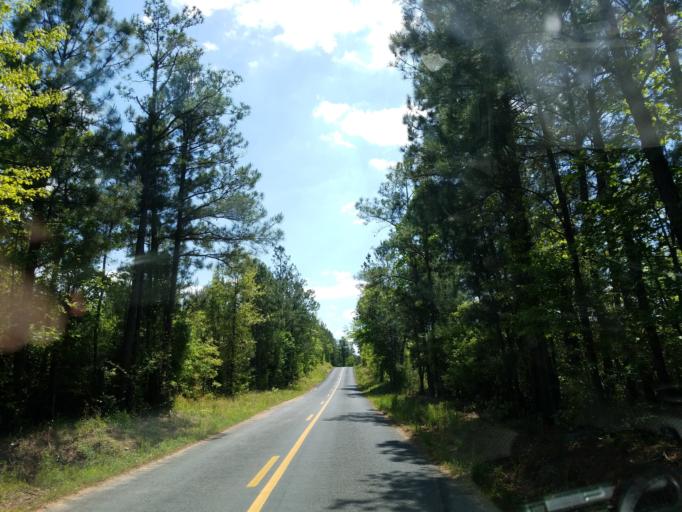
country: US
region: Georgia
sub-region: Butts County
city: Indian Springs
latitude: 33.1482
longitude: -84.0064
